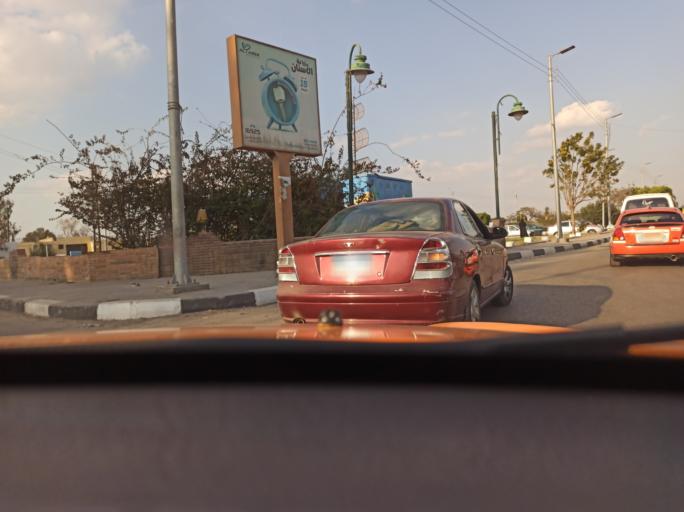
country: EG
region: Al Isma'iliyah
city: Ismailia
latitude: 30.6141
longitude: 32.2487
